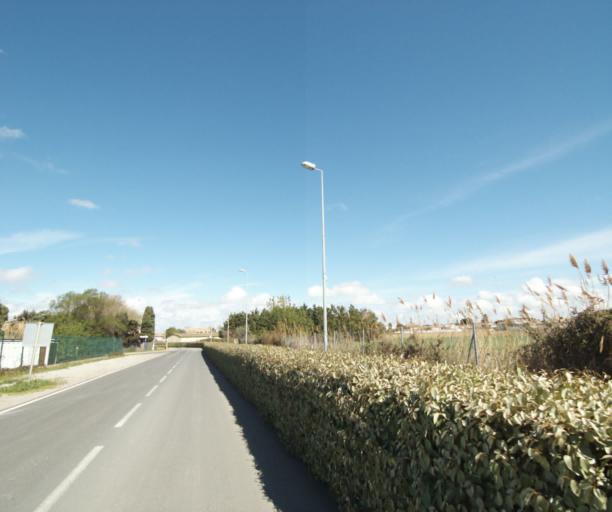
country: FR
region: Languedoc-Roussillon
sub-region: Departement de l'Herault
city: Villeneuve-les-Maguelone
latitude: 43.5309
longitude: 3.8660
